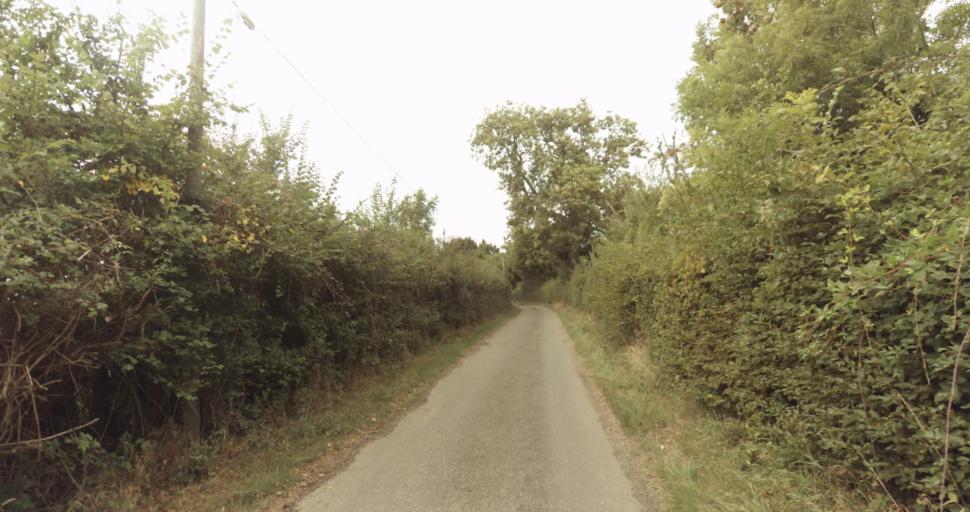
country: FR
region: Lower Normandy
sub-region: Departement de l'Orne
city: Gace
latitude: 48.8332
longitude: 0.3028
